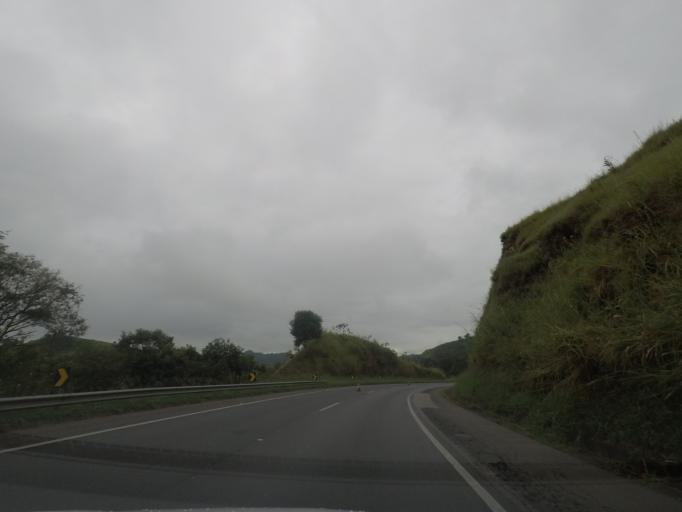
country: BR
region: Sao Paulo
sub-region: Cajati
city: Cajati
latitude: -24.7986
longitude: -48.2111
